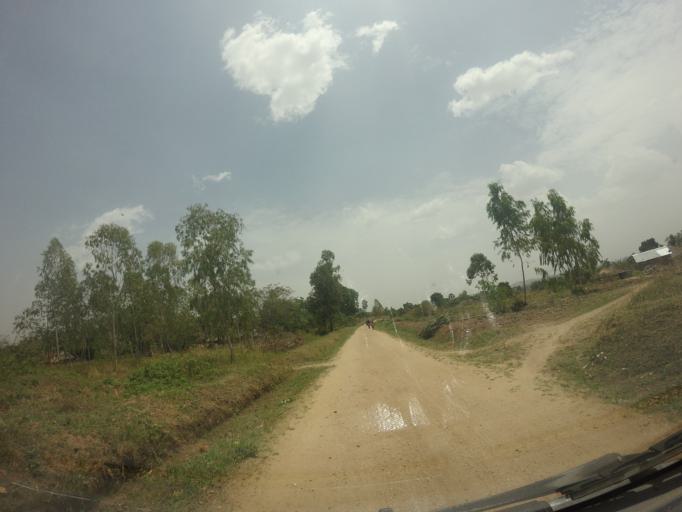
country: UG
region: Northern Region
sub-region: Arua District
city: Arua
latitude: 2.9412
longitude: 30.9144
